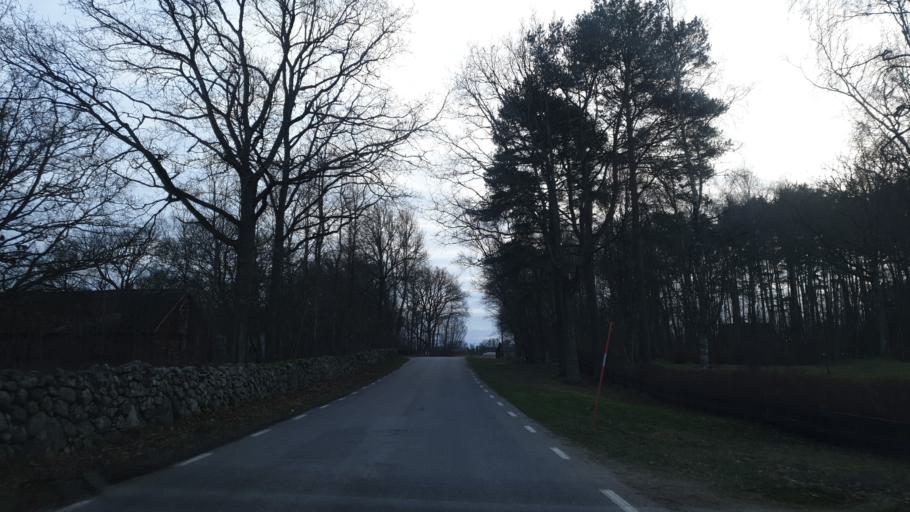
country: SE
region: Blekinge
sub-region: Karlskrona Kommun
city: Jaemjoe
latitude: 56.1966
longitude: 15.9495
